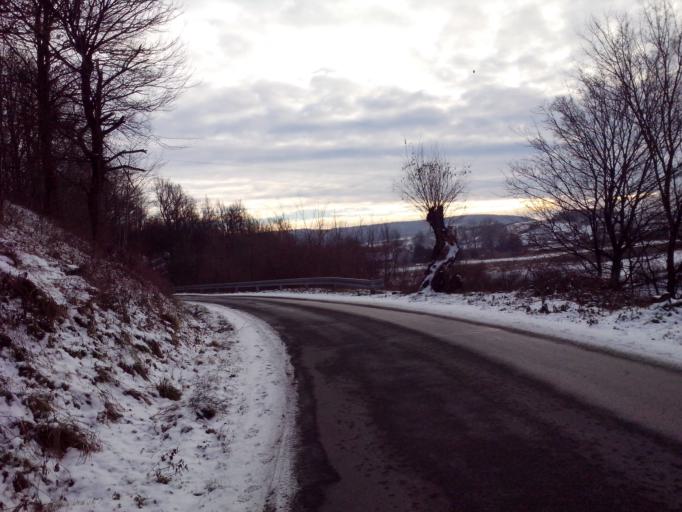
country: PL
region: Subcarpathian Voivodeship
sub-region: Powiat strzyzowski
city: Strzyzow
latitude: 49.8633
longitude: 21.7998
